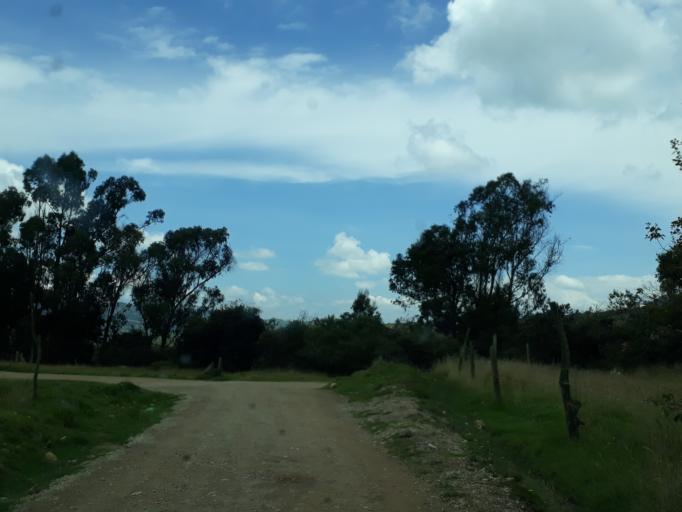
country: CO
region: Cundinamarca
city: Lenguazaque
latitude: 5.3139
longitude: -73.6293
